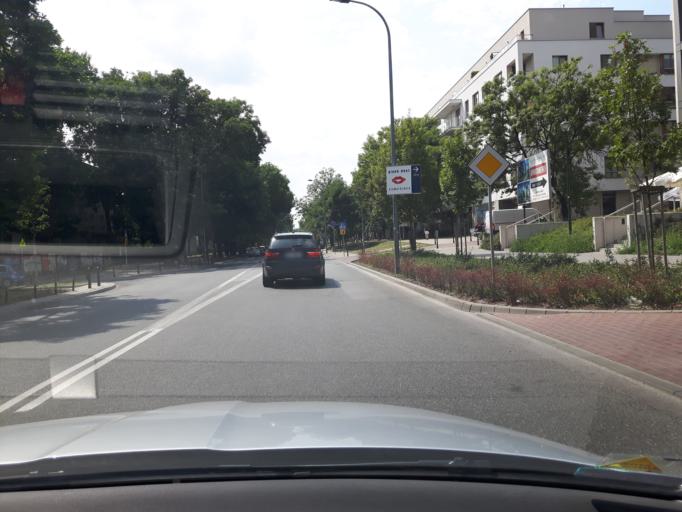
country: PL
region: Masovian Voivodeship
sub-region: Warszawa
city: Mokotow
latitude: 52.1730
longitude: 20.9994
